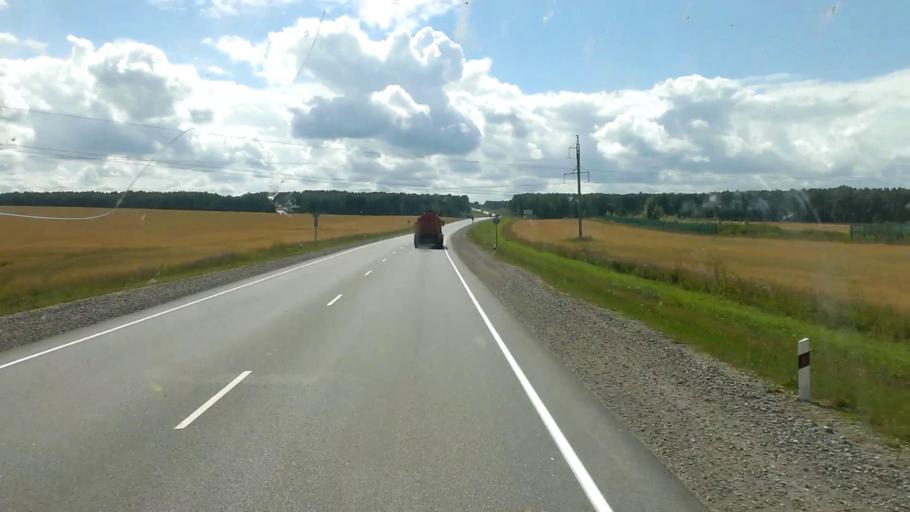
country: RU
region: Altai Krai
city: Troitskoye
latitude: 52.9899
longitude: 84.7427
